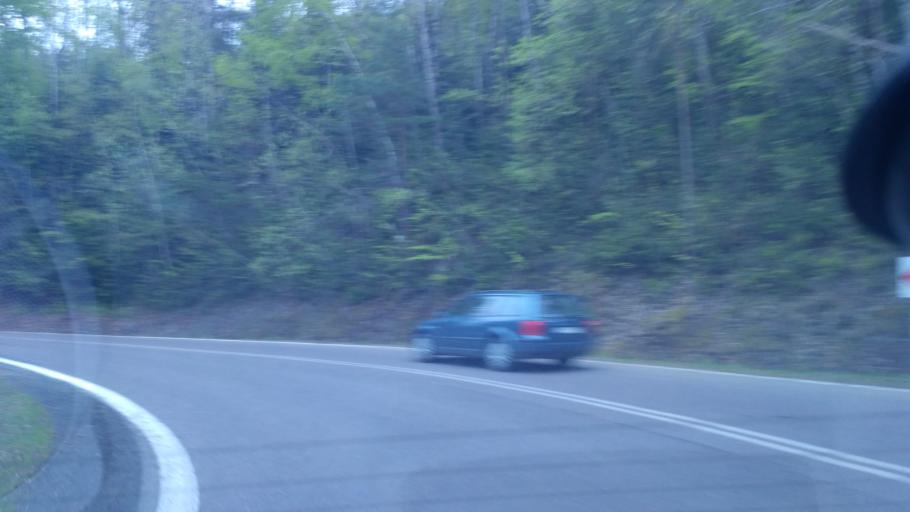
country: PL
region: Subcarpathian Voivodeship
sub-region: Powiat sanocki
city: Tyrawa Woloska
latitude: 49.5648
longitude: 22.3399
